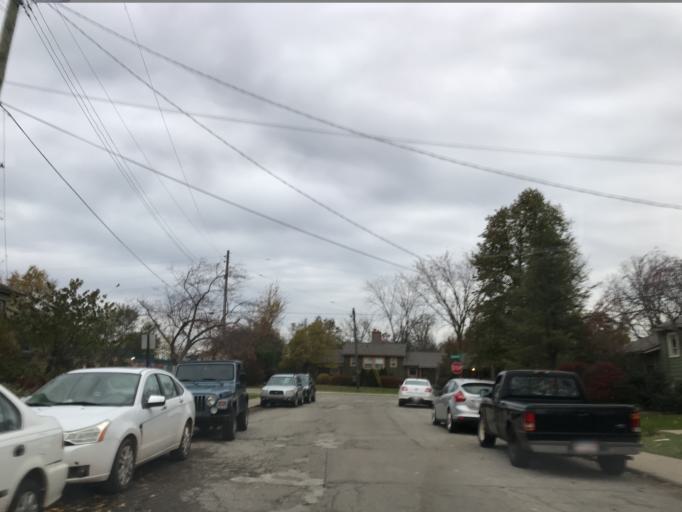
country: US
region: Michigan
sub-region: Washtenaw County
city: Ann Arbor
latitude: 42.2487
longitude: -83.6909
